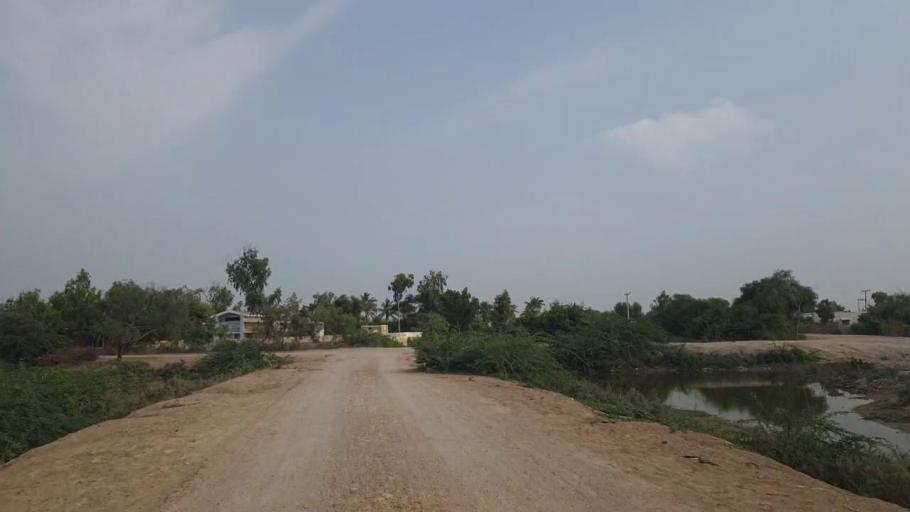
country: PK
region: Sindh
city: Badin
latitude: 24.5927
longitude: 68.7408
